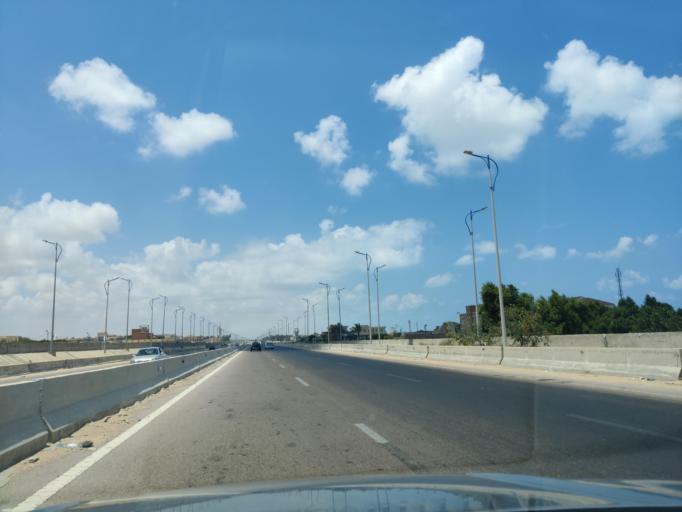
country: EG
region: Alexandria
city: Alexandria
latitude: 30.9580
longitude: 29.5375
